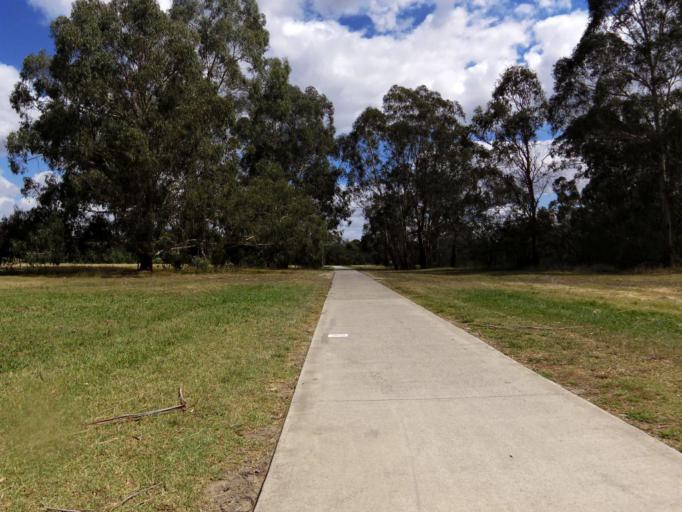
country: AU
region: Victoria
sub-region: Nillumbik
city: Eltham North
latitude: -37.6841
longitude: 145.1529
